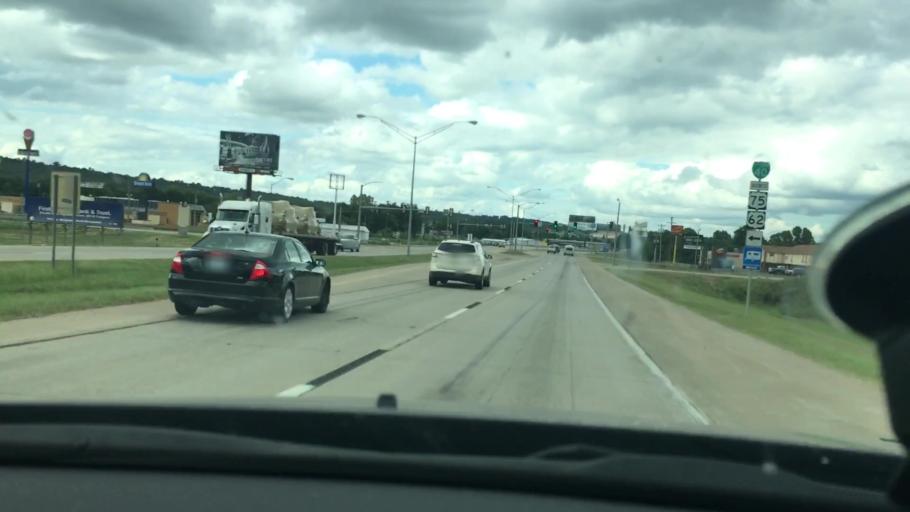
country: US
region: Oklahoma
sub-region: Okmulgee County
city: Henryetta
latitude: 35.4385
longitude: -95.9704
